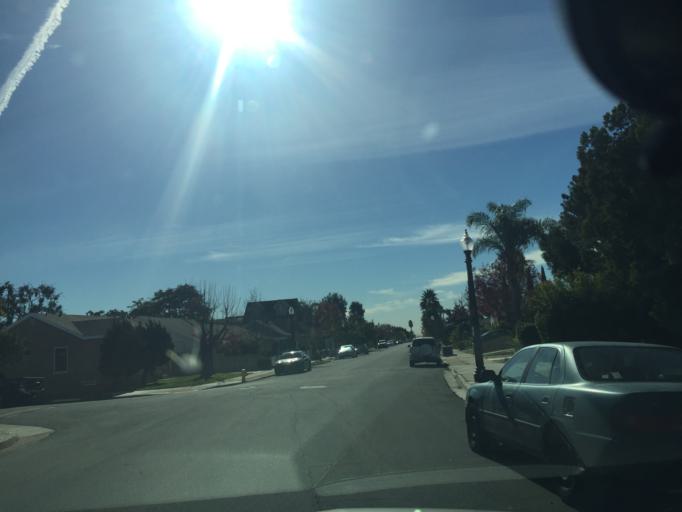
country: US
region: California
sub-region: San Diego County
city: Lemon Grove
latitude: 32.7653
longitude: -117.0880
